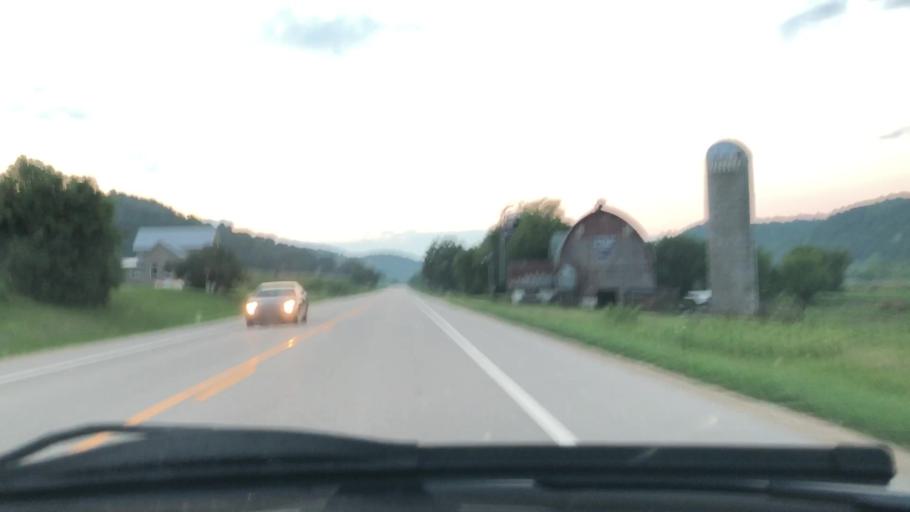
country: US
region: Wisconsin
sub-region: Richland County
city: Richland Center
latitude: 43.3451
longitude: -90.5397
